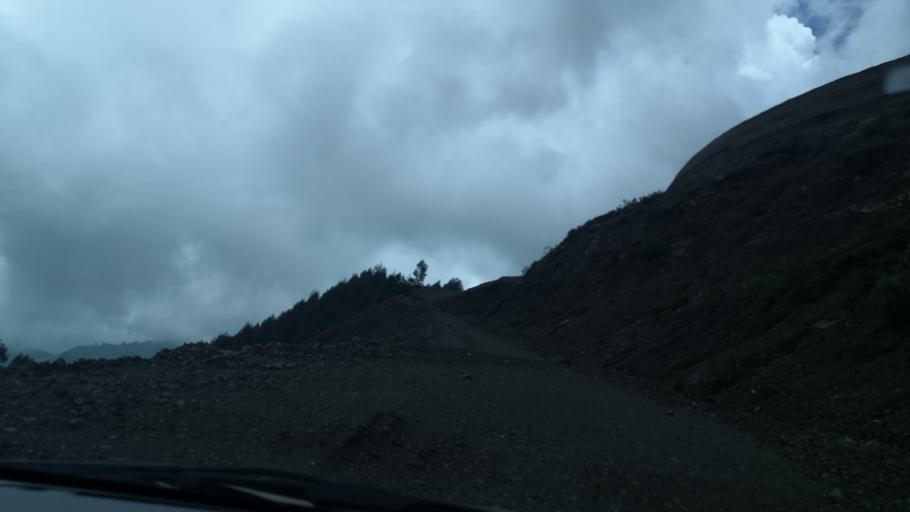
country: ET
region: Amhara
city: Kemise
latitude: 10.3388
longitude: 39.8200
